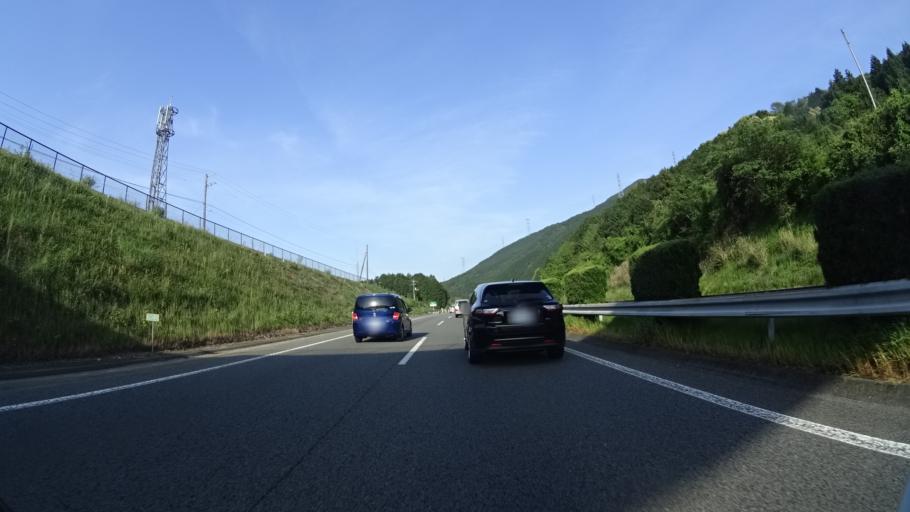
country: JP
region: Ehime
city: Niihama
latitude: 33.9352
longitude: 133.3686
